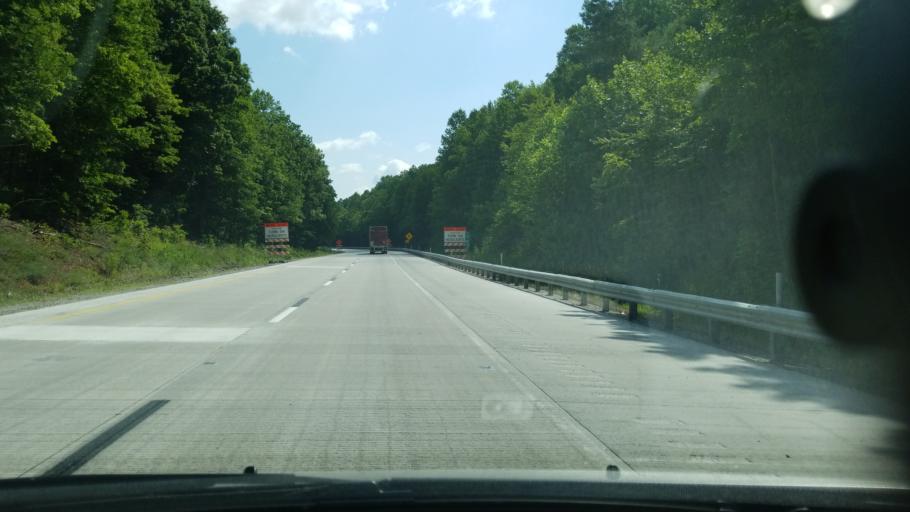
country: US
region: Pennsylvania
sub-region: Schuylkill County
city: Pine Grove
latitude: 40.5242
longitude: -76.4396
